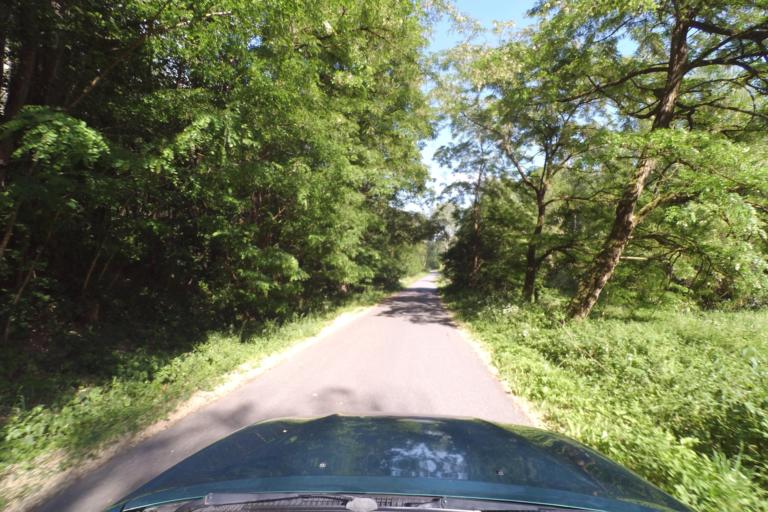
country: CZ
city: Osecna
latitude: 50.6717
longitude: 14.8685
